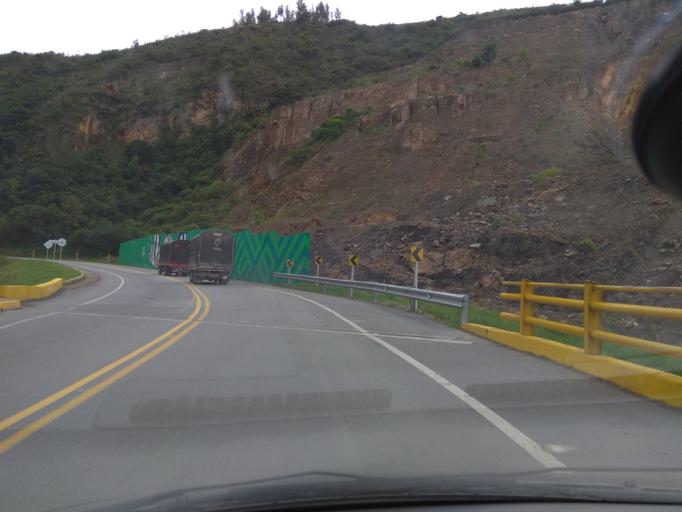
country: CO
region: Boyaca
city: Duitama
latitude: 5.8528
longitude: -73.0119
